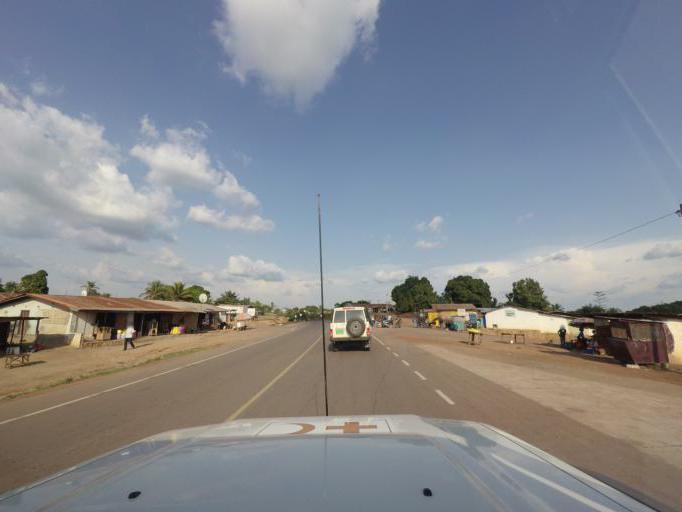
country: LR
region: Bong
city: Gbarnga
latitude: 6.9924
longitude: -9.4569
